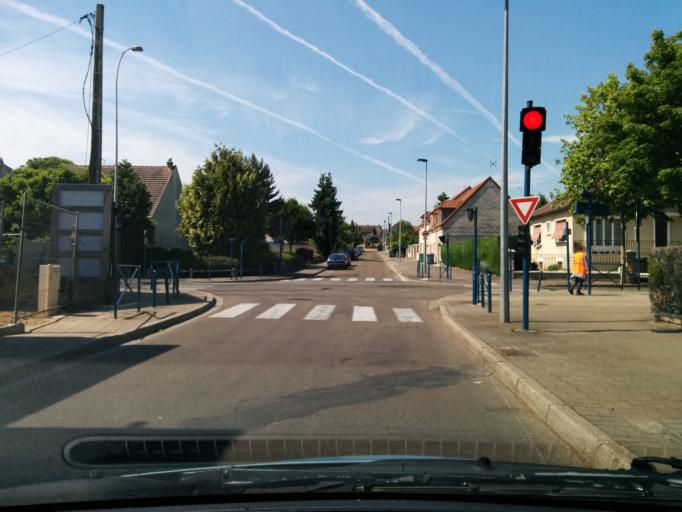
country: FR
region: Ile-de-France
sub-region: Departement des Yvelines
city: Mantes-la-Jolie
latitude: 49.0004
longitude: 1.7019
